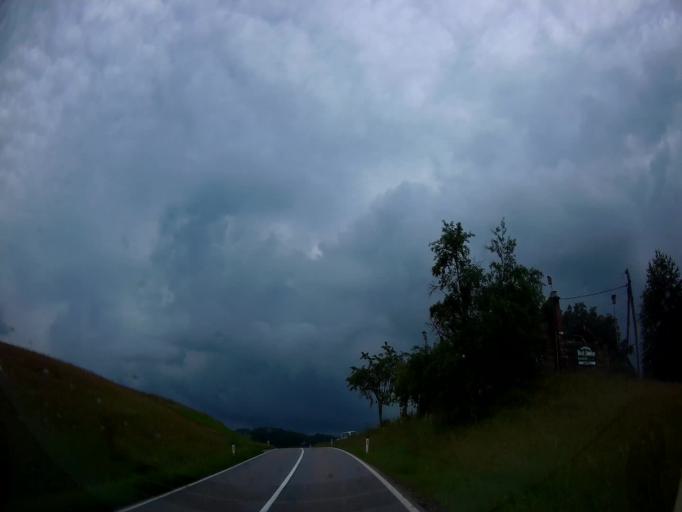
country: AT
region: Salzburg
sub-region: Politischer Bezirk Salzburg-Umgebung
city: Mattsee
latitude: 48.0315
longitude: 13.1424
